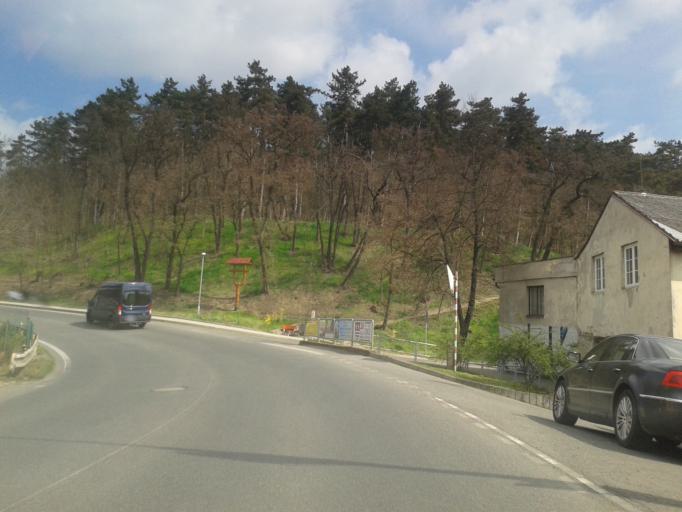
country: CZ
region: Central Bohemia
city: Zdice
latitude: 49.9160
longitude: 13.9839
